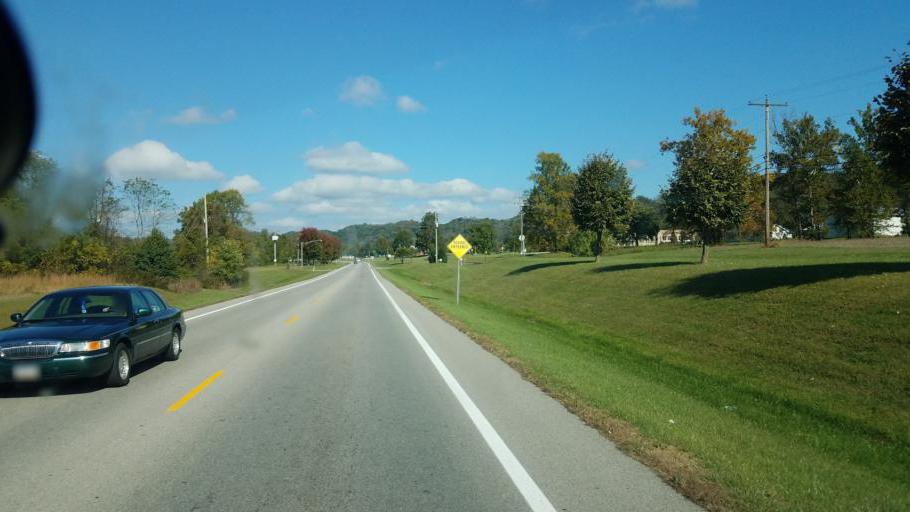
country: US
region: Ohio
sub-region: Brown County
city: Aberdeen
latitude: 38.6773
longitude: -83.7736
